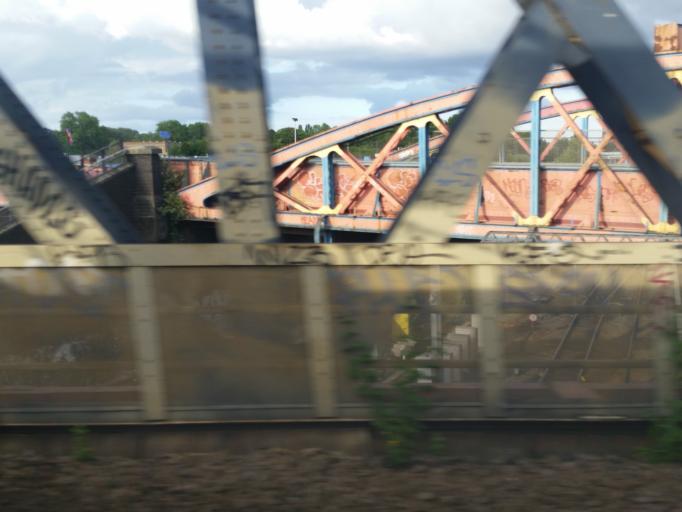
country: GB
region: England
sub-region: Greater London
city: Hammersmith
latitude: 51.5256
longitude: -0.2348
